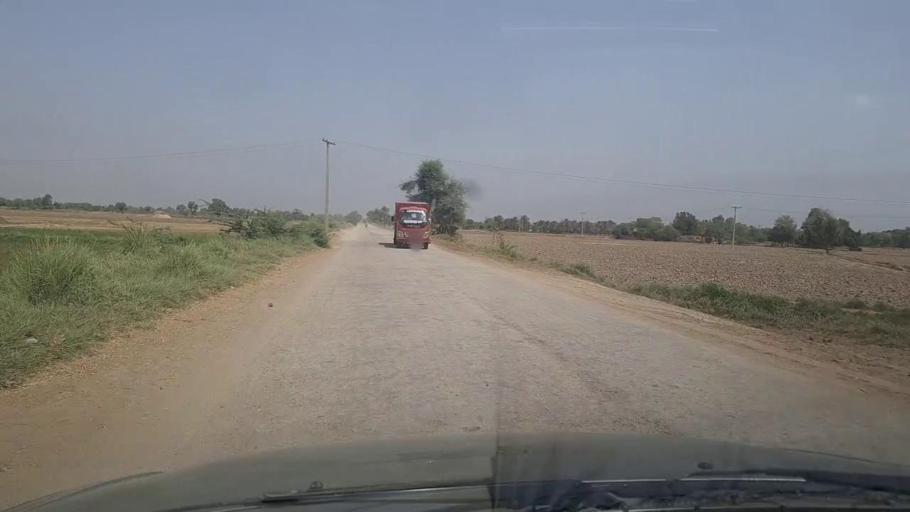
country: PK
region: Sindh
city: Setharja Old
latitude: 27.1351
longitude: 68.5301
